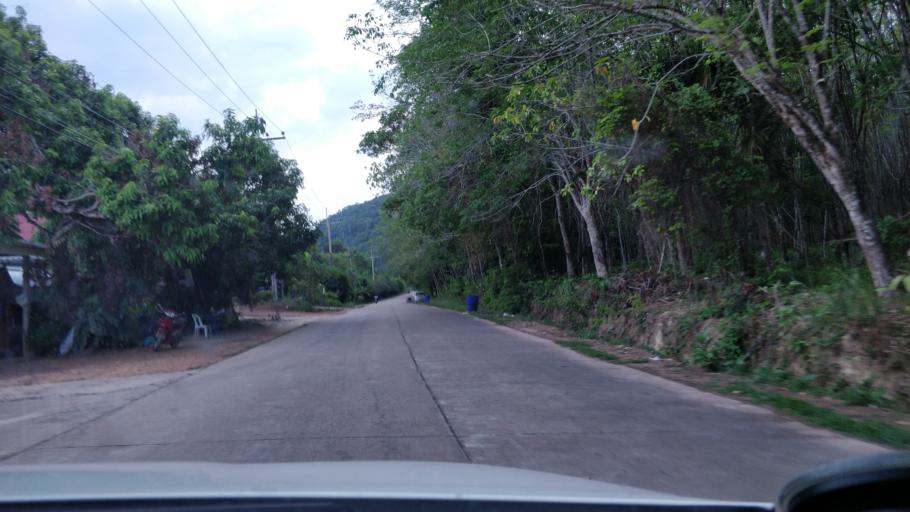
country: TH
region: Krabi
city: Saladan
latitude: 7.5868
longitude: 99.0690
